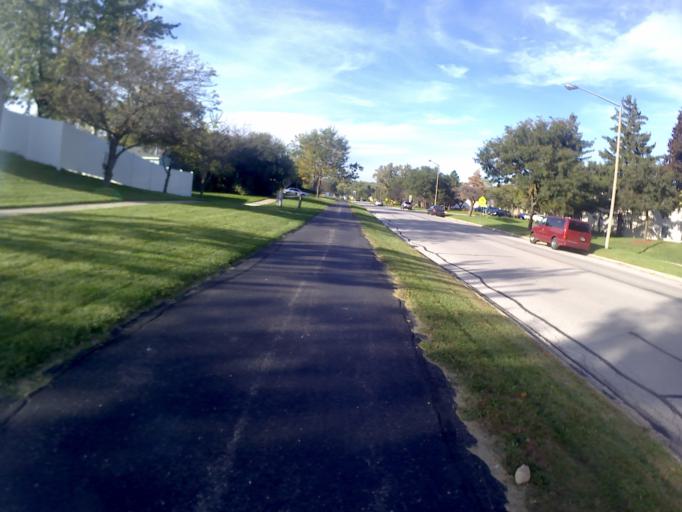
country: US
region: Illinois
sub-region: DuPage County
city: Woodridge
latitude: 41.7405
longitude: -88.0475
